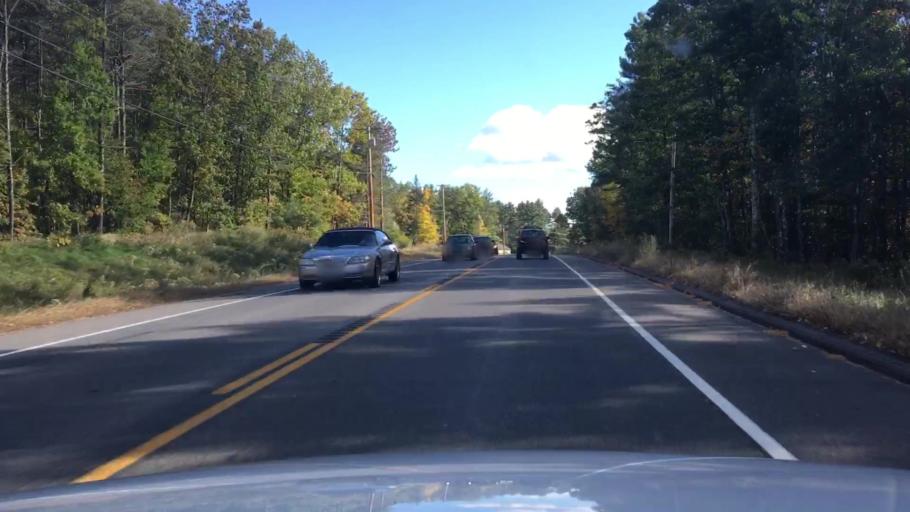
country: US
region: Maine
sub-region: York County
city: South Sanford
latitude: 43.3692
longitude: -70.6718
